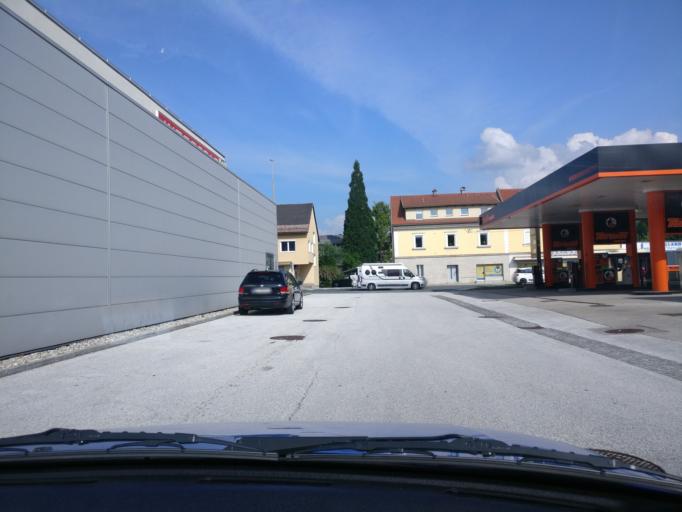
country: AT
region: Carinthia
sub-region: Klagenfurt am Woerthersee
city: Klagenfurt am Woerthersee
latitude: 46.6091
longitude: 14.2990
